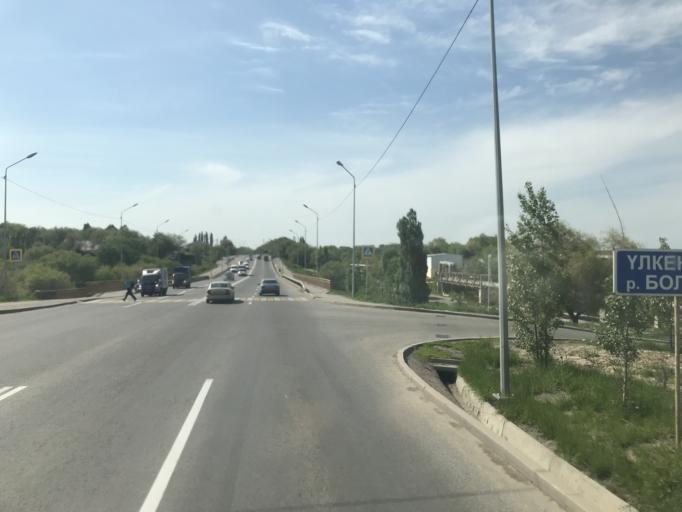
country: KZ
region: Almaty Oblysy
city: Burunday
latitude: 43.3100
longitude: 76.8700
